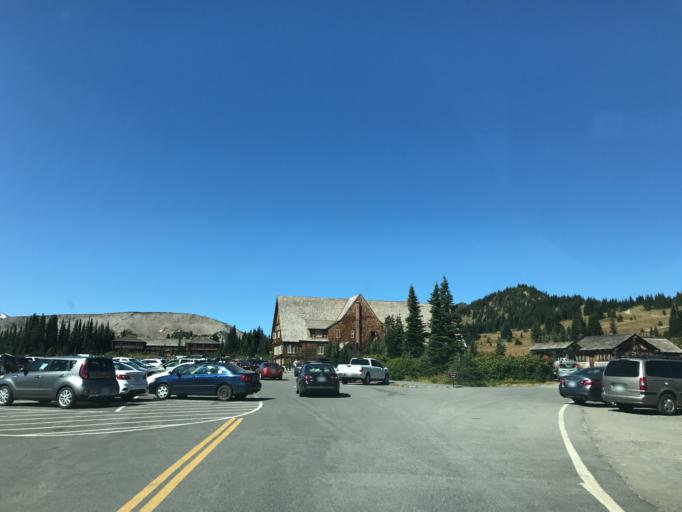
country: US
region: Washington
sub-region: King County
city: Enumclaw
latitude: 46.9145
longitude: -121.6399
